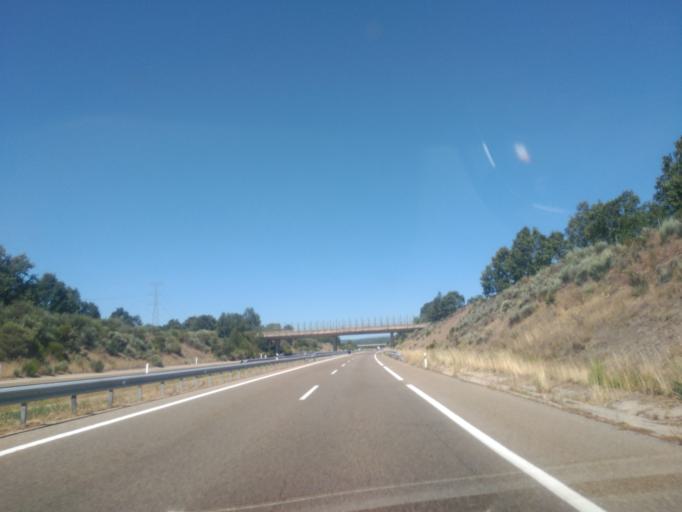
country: ES
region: Castille and Leon
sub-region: Provincia de Zamora
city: Cernadilla
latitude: 42.0312
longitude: -6.4230
